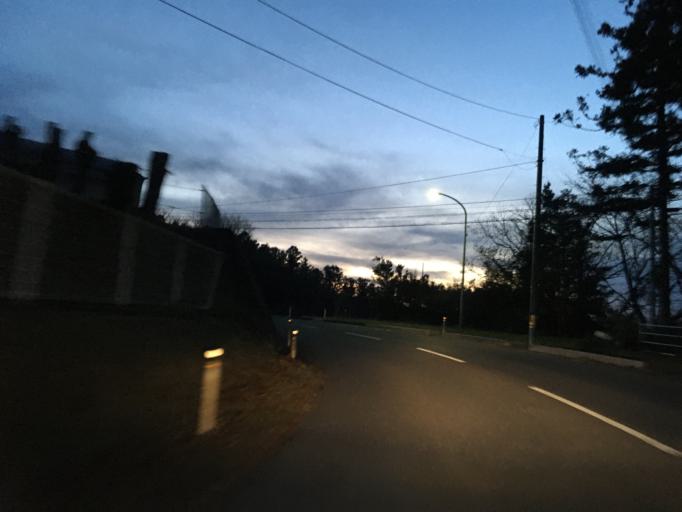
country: JP
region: Miyagi
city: Wakuya
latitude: 38.7019
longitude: 141.1597
